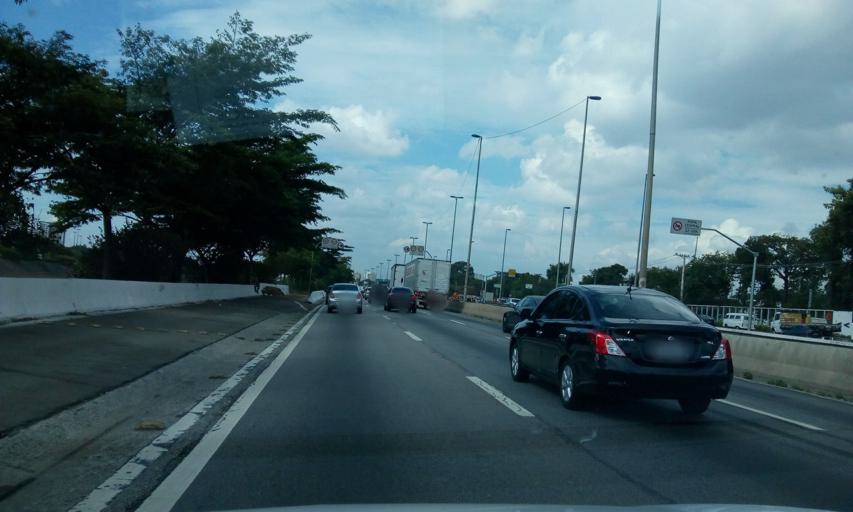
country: BR
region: Sao Paulo
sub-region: Osasco
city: Osasco
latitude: -23.5089
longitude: -46.7133
